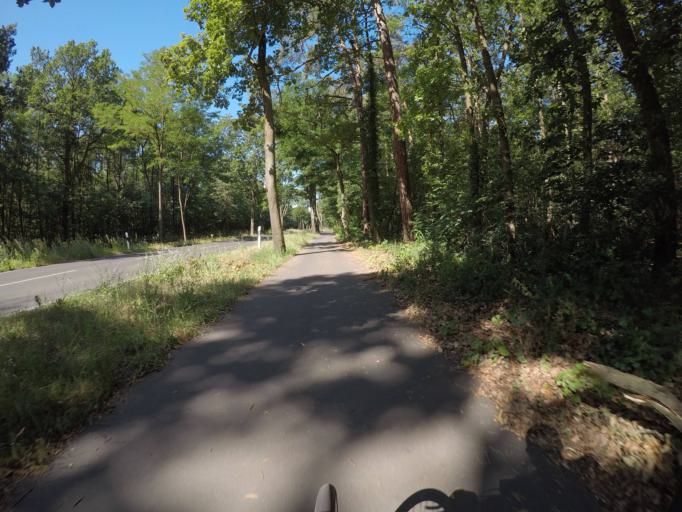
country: DE
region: Brandenburg
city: Schoneiche
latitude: 52.4671
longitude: 13.6704
